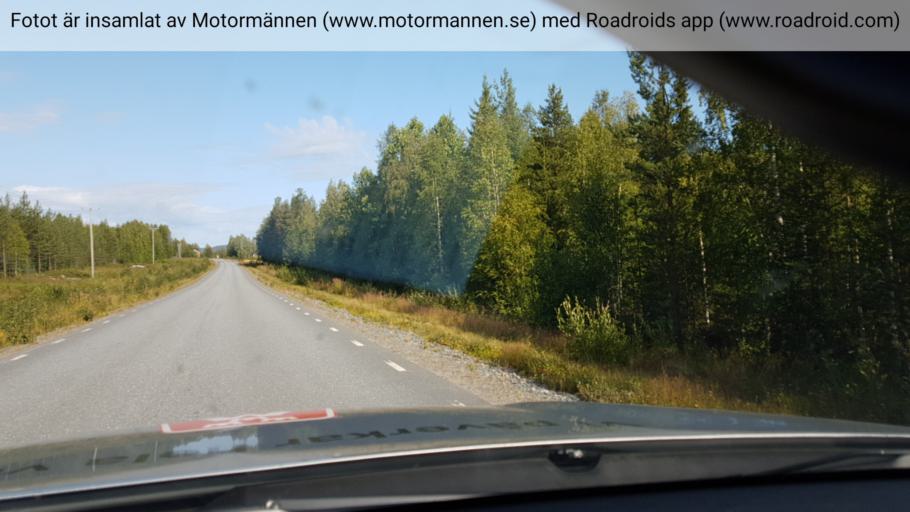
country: SE
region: Norrbotten
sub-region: Alvsbyns Kommun
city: AElvsbyn
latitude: 65.6330
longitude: 20.9018
